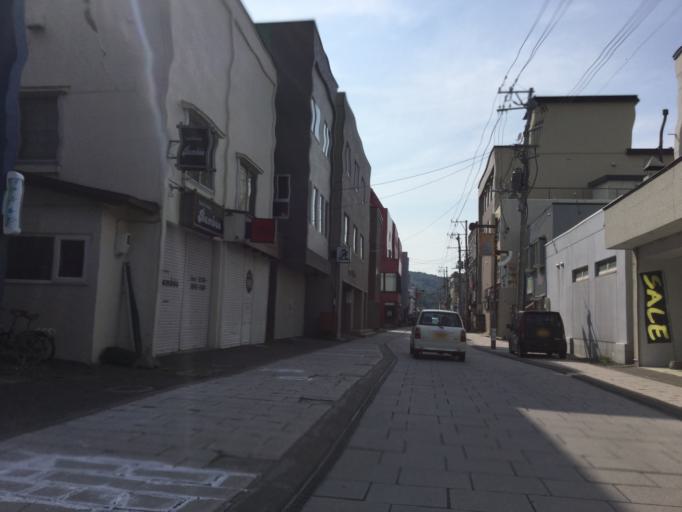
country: JP
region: Hokkaido
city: Wakkanai
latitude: 45.3973
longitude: 141.6872
